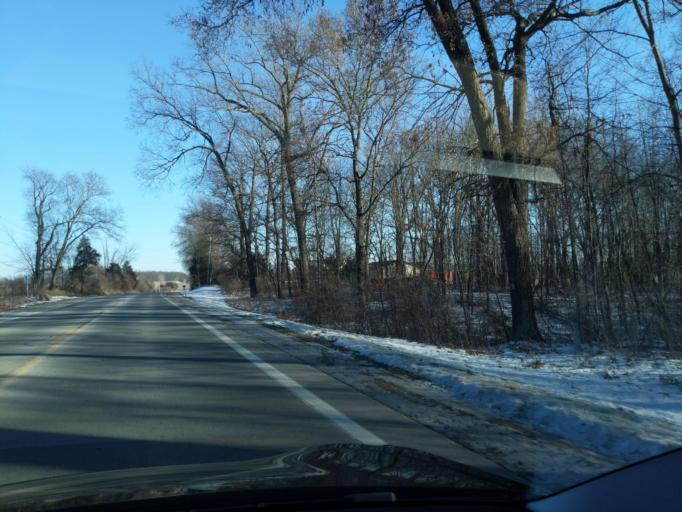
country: US
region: Michigan
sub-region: Ingham County
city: Leslie
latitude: 42.3949
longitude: -84.3110
